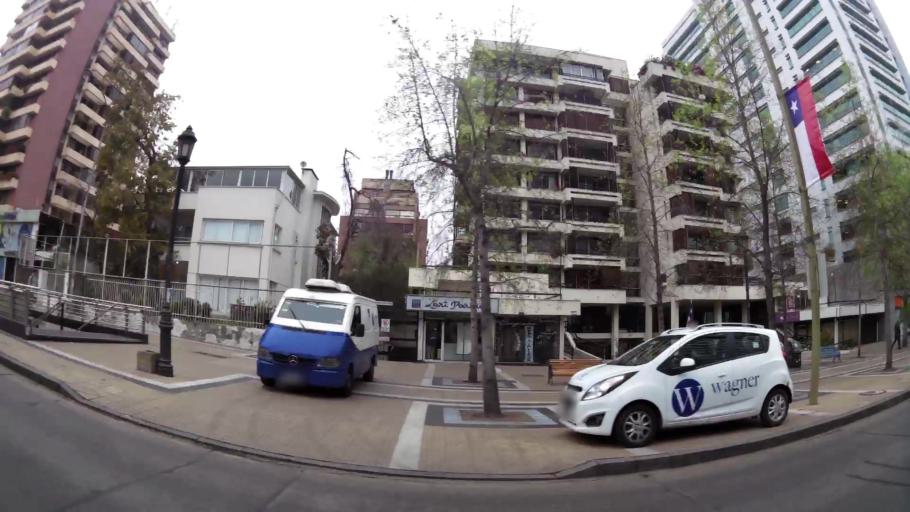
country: CL
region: Santiago Metropolitan
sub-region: Provincia de Santiago
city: Villa Presidente Frei, Nunoa, Santiago, Chile
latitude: -33.4168
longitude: -70.5964
